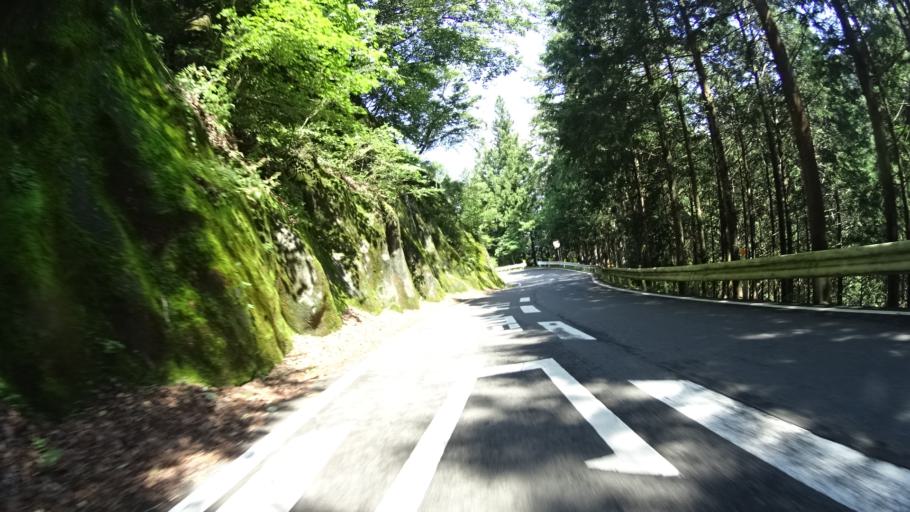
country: JP
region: Gunma
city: Tomioka
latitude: 36.0615
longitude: 138.8335
